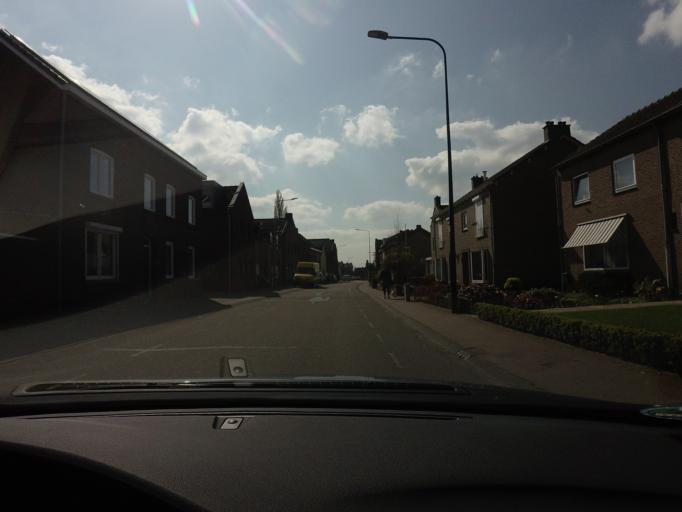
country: NL
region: Limburg
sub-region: Eijsden-Margraten
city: Eijsden
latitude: 50.8069
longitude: 5.7331
